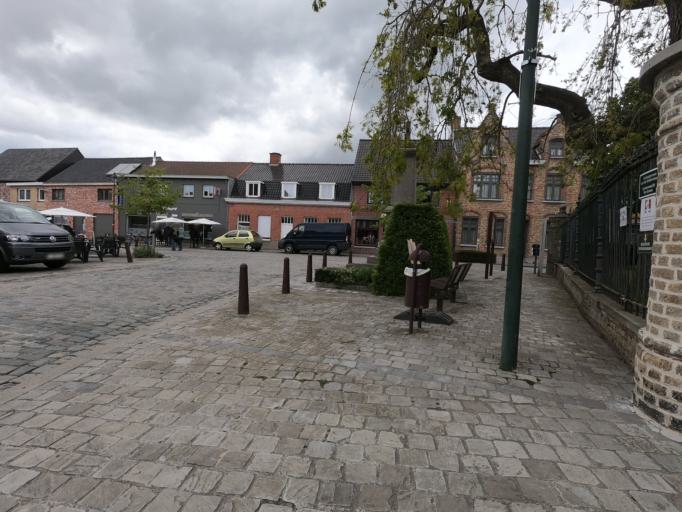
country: BE
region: Flanders
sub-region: Provincie West-Vlaanderen
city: Poperinge
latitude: 50.9337
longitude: 2.7413
